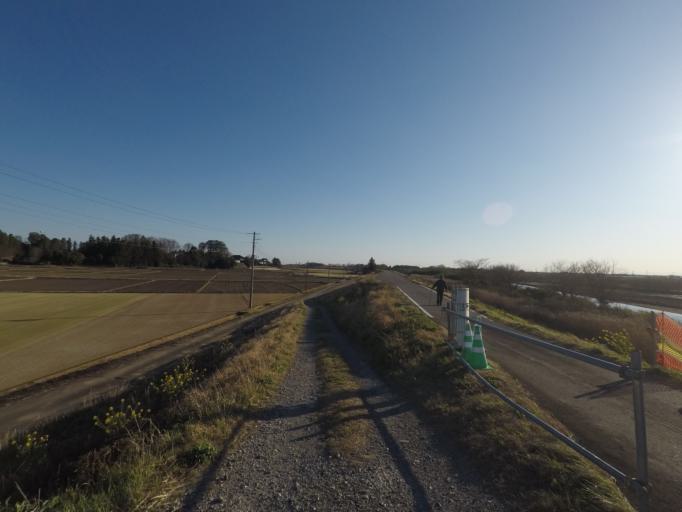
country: JP
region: Ibaraki
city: Ishige
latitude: 36.1603
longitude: 140.0068
